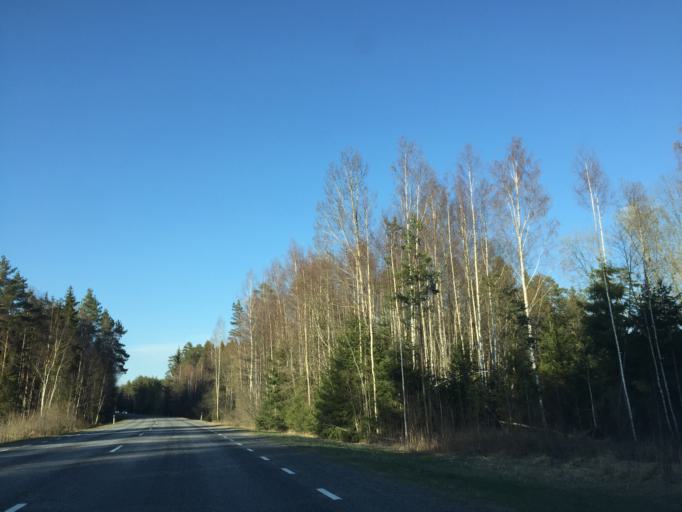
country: EE
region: Valgamaa
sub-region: Torva linn
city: Torva
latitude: 58.0966
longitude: 26.1068
